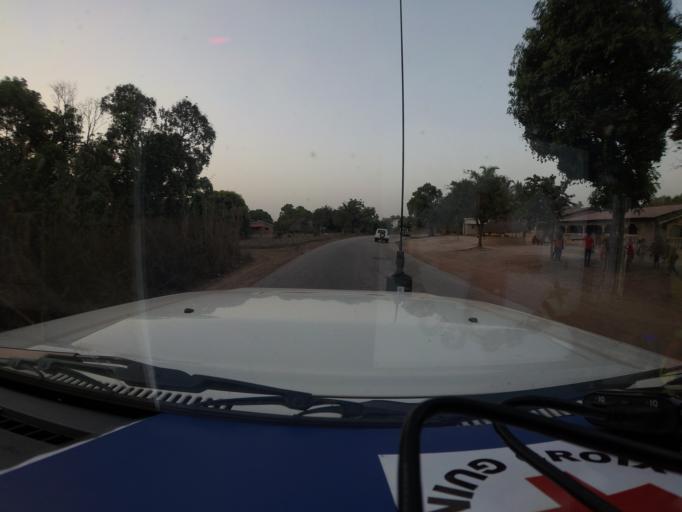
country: GN
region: Kindia
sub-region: Kindia
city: Kindia
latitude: 9.8883
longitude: -13.0552
